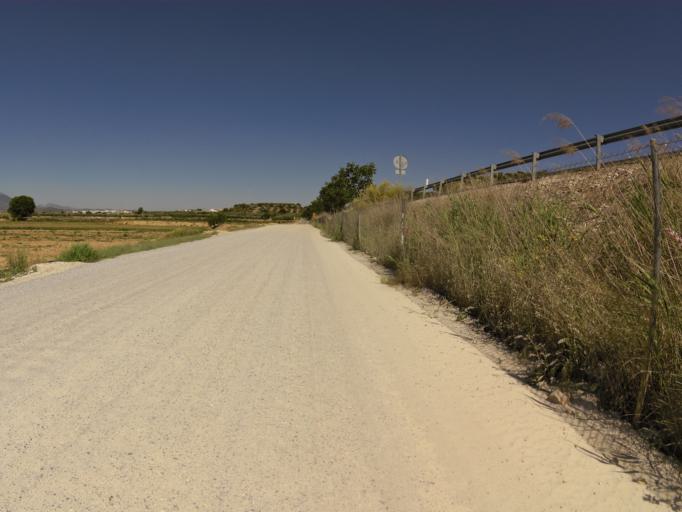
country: ES
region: Andalusia
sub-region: Provincia de Granada
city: Huetor-Tajar
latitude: 37.1811
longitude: -4.0537
